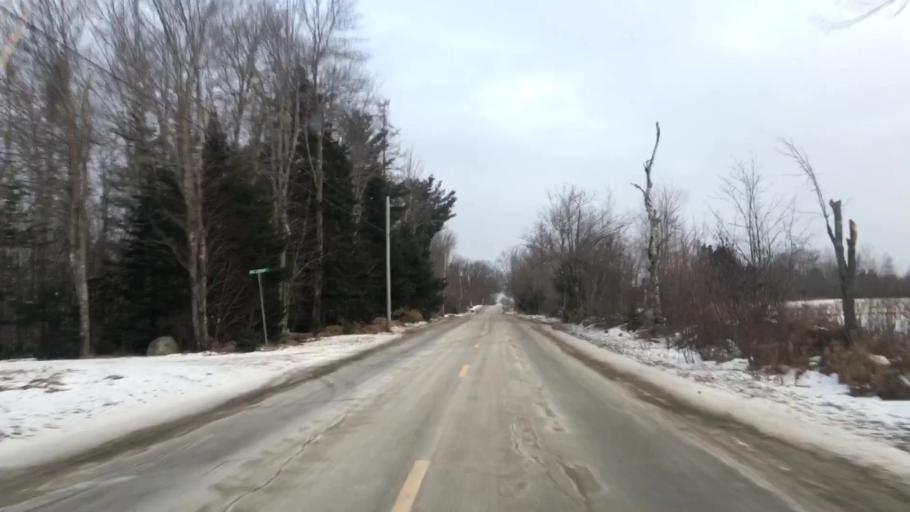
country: US
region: Maine
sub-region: Hancock County
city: Franklin
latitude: 44.7048
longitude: -68.3408
